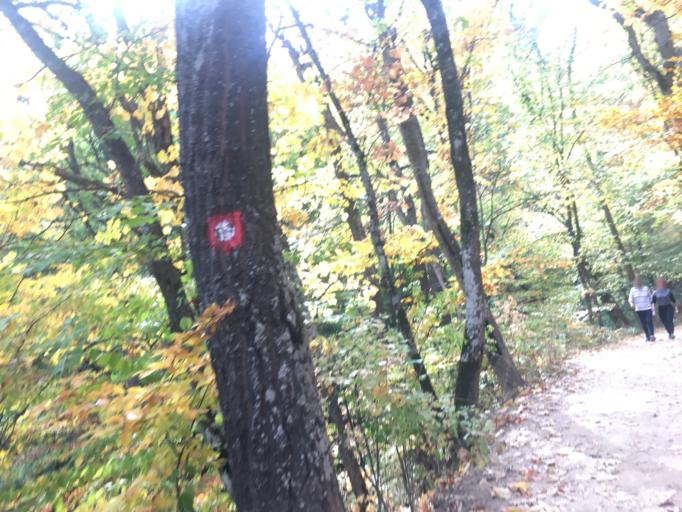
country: XK
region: Pristina
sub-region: Komuna e Prishtines
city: Pristina
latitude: 42.6681
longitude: 21.2180
